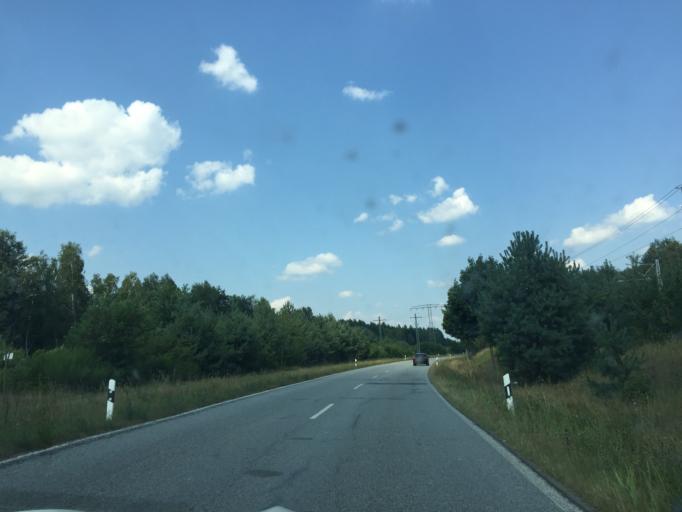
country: DE
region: Saxony
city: Boxberg
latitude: 51.4305
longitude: 14.5273
